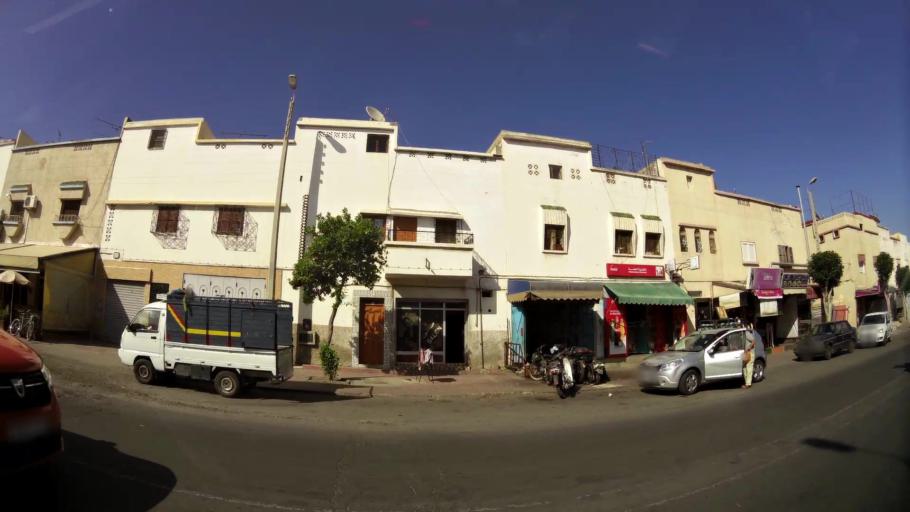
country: MA
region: Oued ed Dahab-Lagouira
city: Dakhla
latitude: 30.4232
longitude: -9.5642
